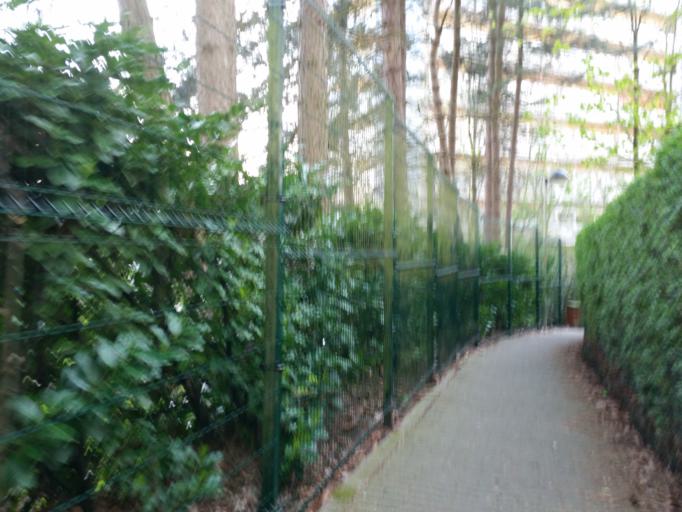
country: BE
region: Flanders
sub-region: Provincie Vlaams-Brabant
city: Dilbeek
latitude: 50.8542
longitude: 4.3010
